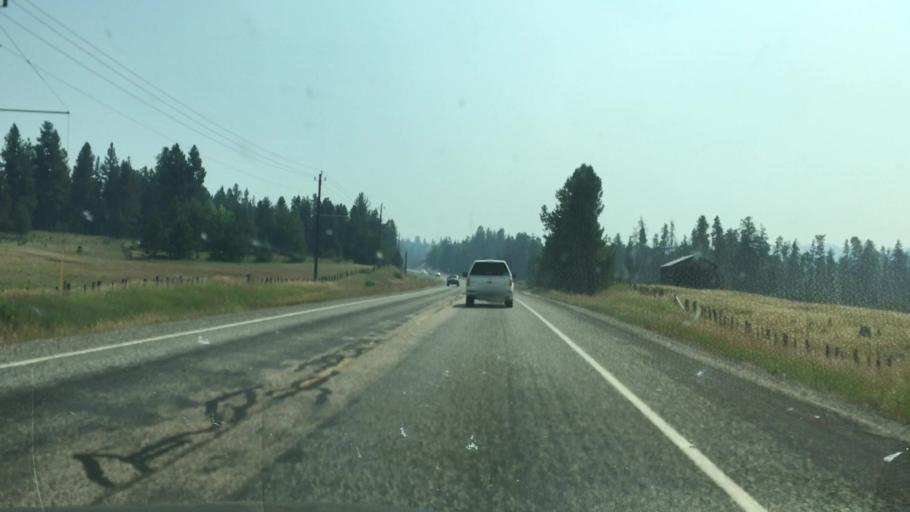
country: US
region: Idaho
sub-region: Valley County
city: Cascade
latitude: 44.3905
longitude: -116.0096
